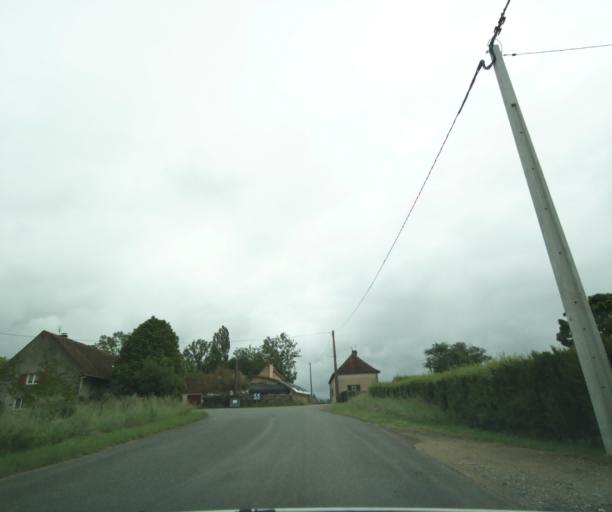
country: FR
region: Bourgogne
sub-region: Departement de Saone-et-Loire
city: Charolles
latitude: 46.4490
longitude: 4.3418
